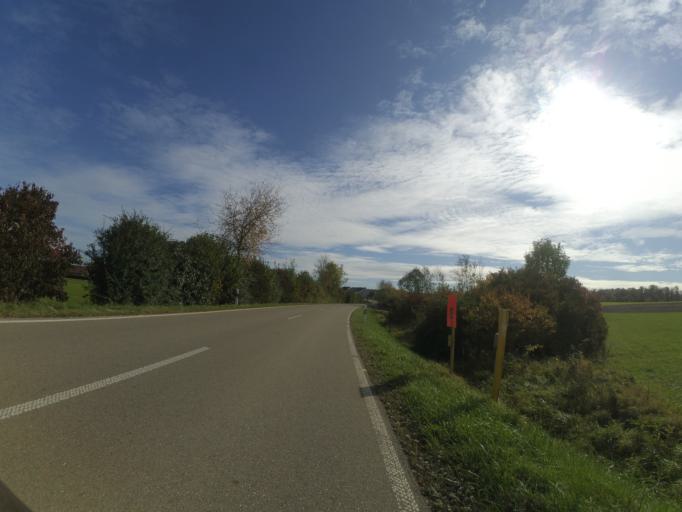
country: DE
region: Baden-Wuerttemberg
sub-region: Tuebingen Region
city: Lonsee
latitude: 48.6055
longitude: 9.9355
